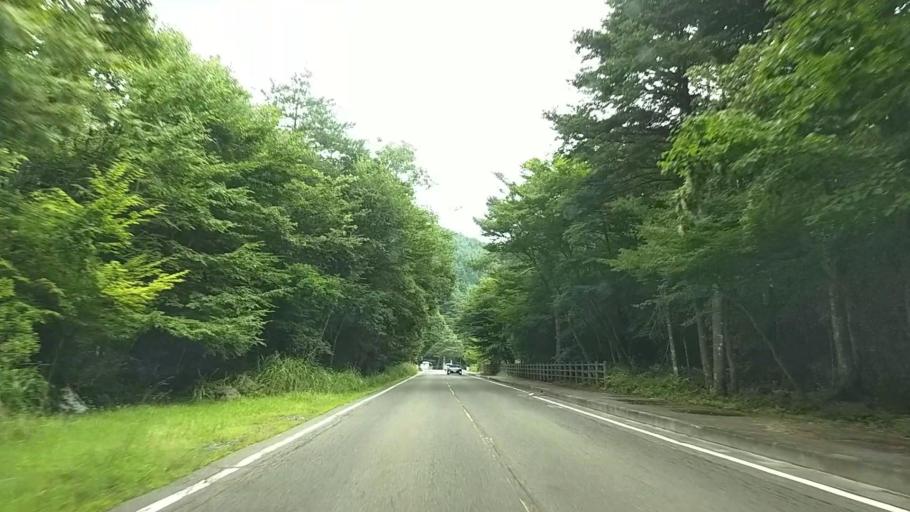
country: JP
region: Yamanashi
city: Fujikawaguchiko
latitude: 35.4974
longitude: 138.6504
